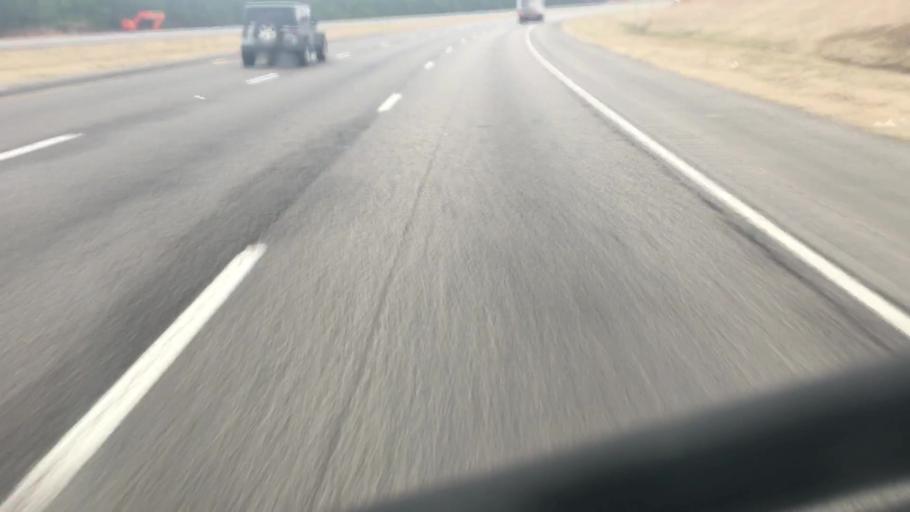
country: US
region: Alabama
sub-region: Walker County
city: Dora
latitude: 33.6664
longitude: -87.0682
